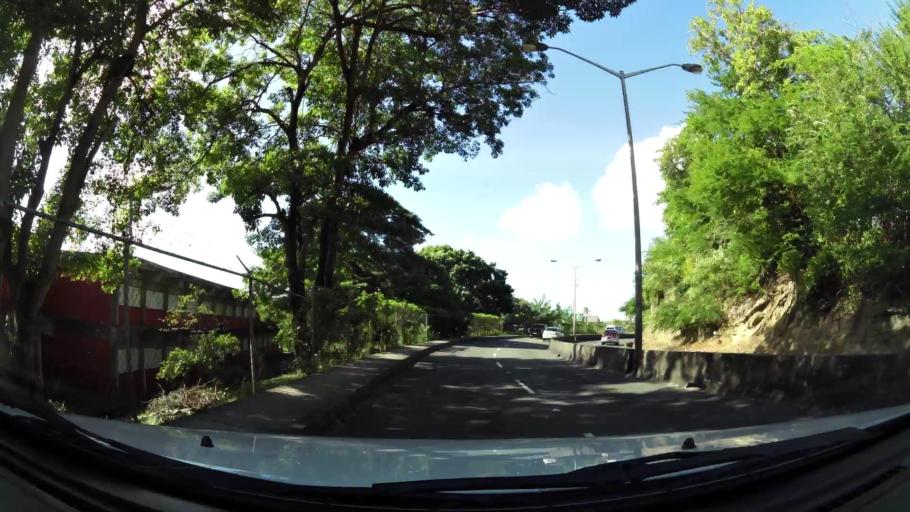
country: LC
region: Castries Quarter
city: Bisee
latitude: 14.0278
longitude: -60.9784
